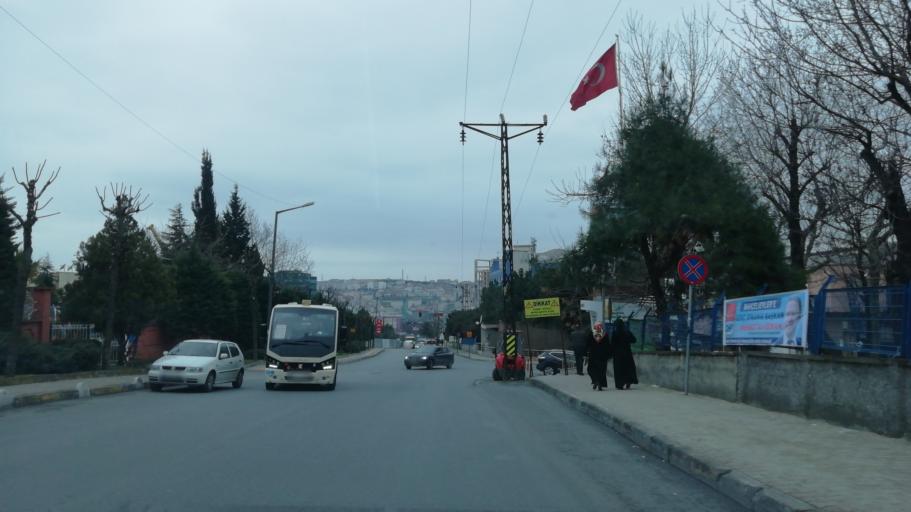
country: TR
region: Istanbul
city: Mahmutbey
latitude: 41.0158
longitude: 28.8197
